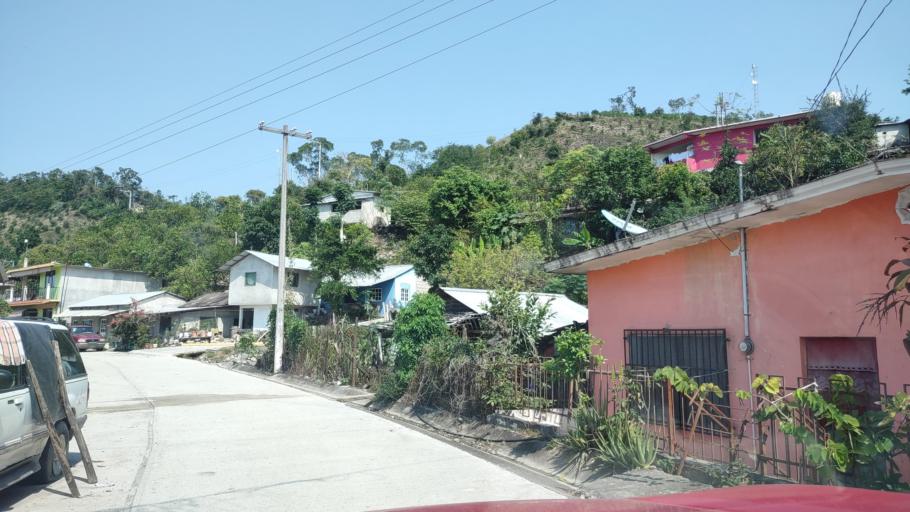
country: MX
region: Veracruz
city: Agua Dulce
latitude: 20.3101
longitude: -97.1703
